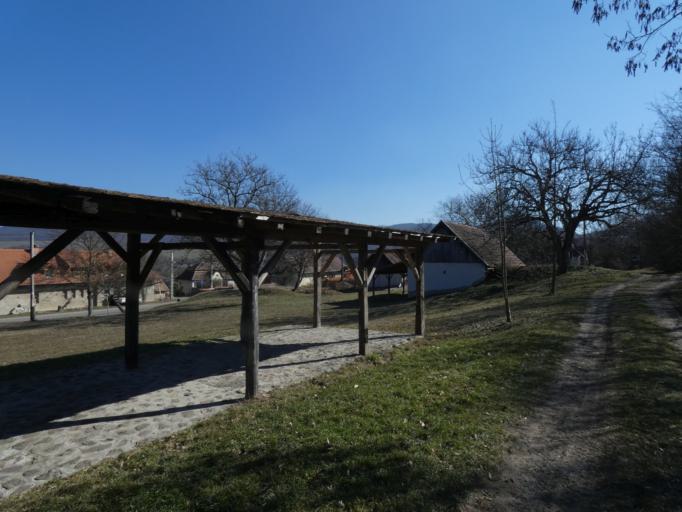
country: HU
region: Pest
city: Szob
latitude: 47.9356
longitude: 18.8193
